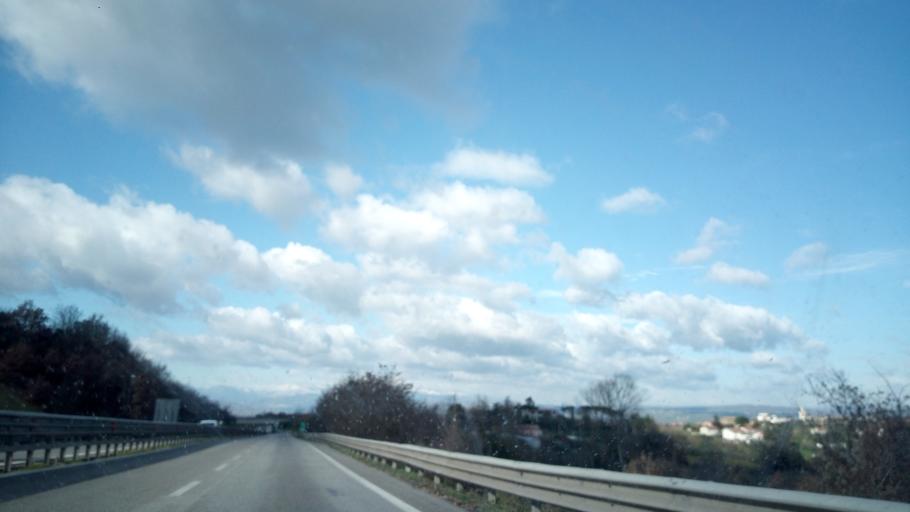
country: IT
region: Campania
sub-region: Provincia di Benevento
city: San Giorgio del Sannio
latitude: 41.0843
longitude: 14.8474
